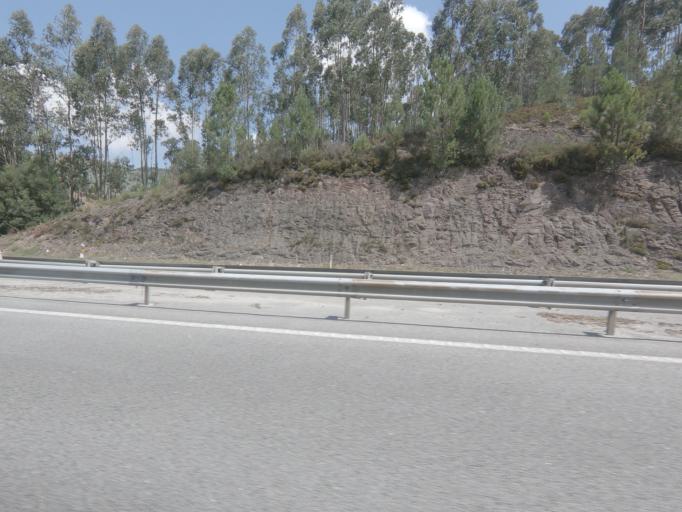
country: PT
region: Porto
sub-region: Paredes
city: Recarei
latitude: 41.1718
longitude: -8.4113
